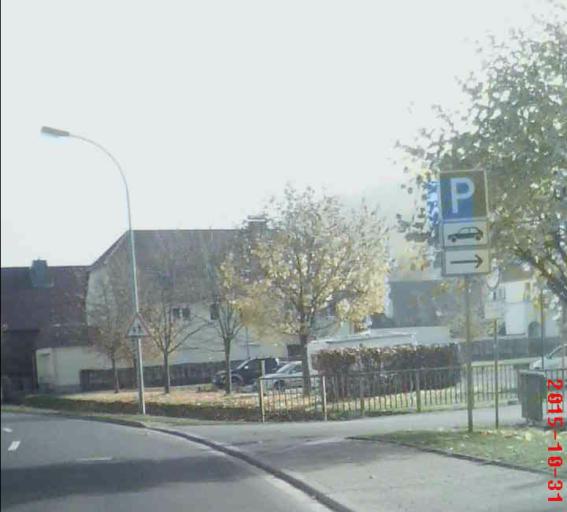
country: DE
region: Thuringia
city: Grossbartloff
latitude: 51.2149
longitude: 10.2193
